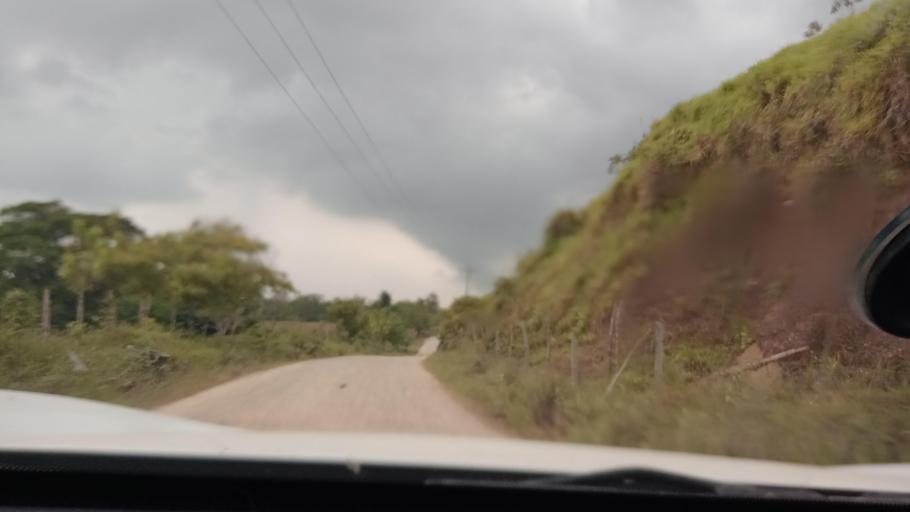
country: MX
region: Tabasco
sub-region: Huimanguillo
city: Francisco Rueda
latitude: 17.4380
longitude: -94.0596
